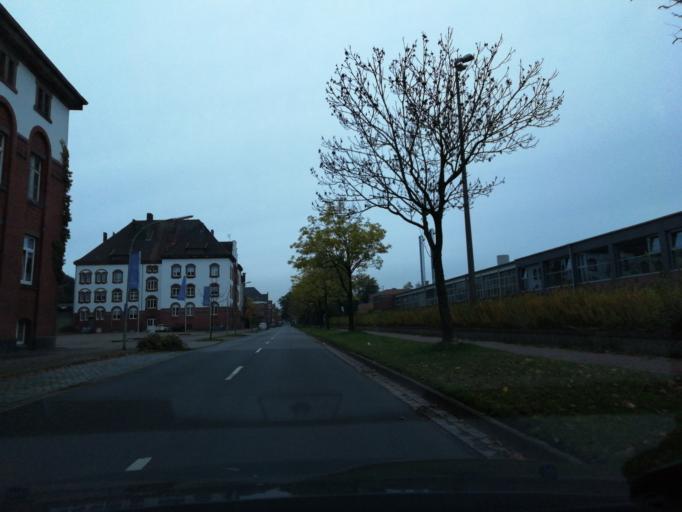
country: DE
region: Lower Saxony
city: Wilhelmshaven
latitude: 53.5174
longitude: 8.1300
